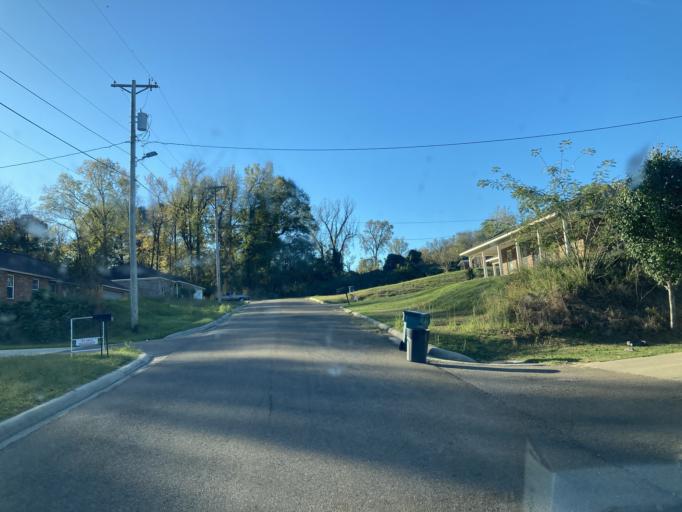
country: US
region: Mississippi
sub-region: Yazoo County
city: Yazoo City
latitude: 32.8484
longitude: -90.4032
